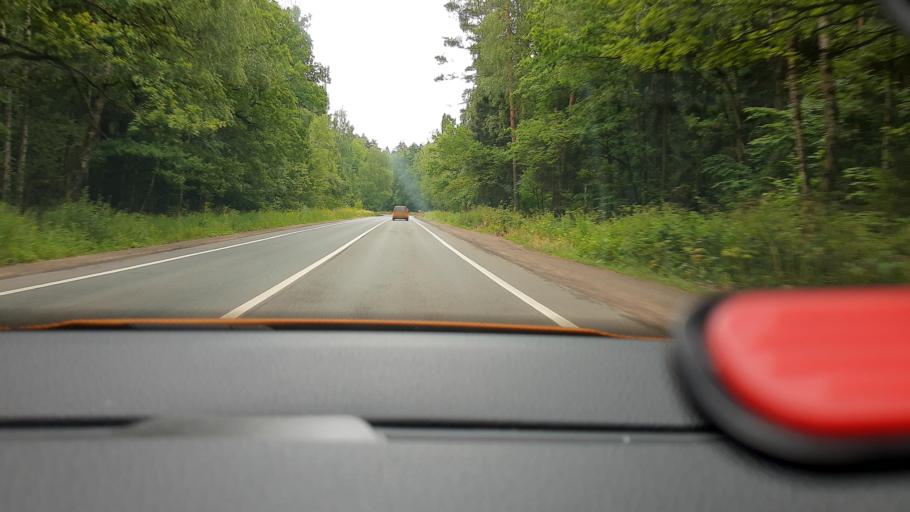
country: RU
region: Moskovskaya
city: Pirogovskiy
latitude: 55.9993
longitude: 37.6884
